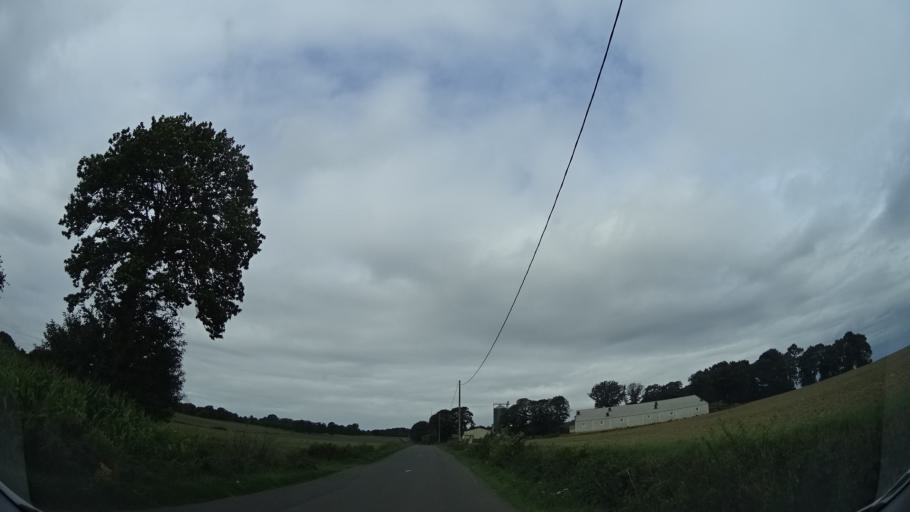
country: FR
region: Brittany
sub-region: Departement d'Ille-et-Vilaine
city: Irodouer
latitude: 48.2853
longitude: -1.9116
